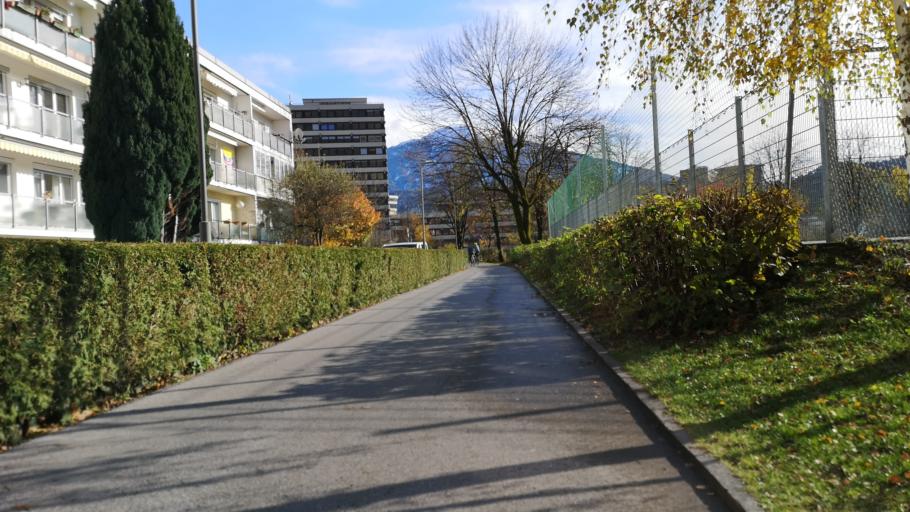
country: AT
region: Tyrol
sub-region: Innsbruck Stadt
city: Innsbruck
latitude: 47.2652
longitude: 11.3823
